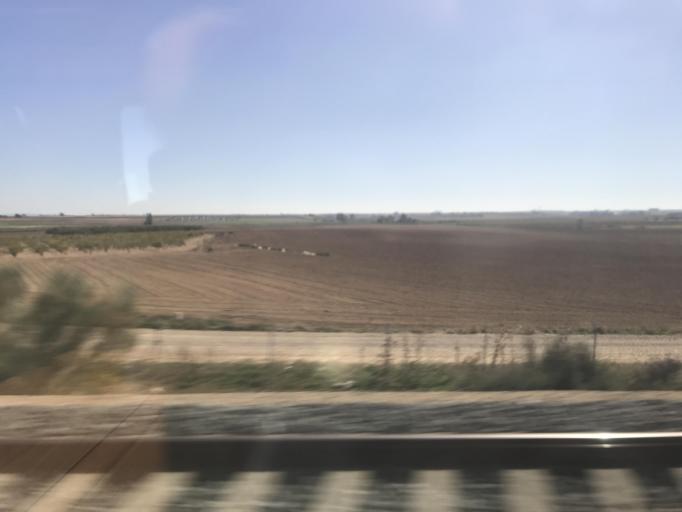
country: ES
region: Castille-La Mancha
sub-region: Province of Toledo
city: Santa Cruz de la Zarza
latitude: 39.9720
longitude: -3.1687
